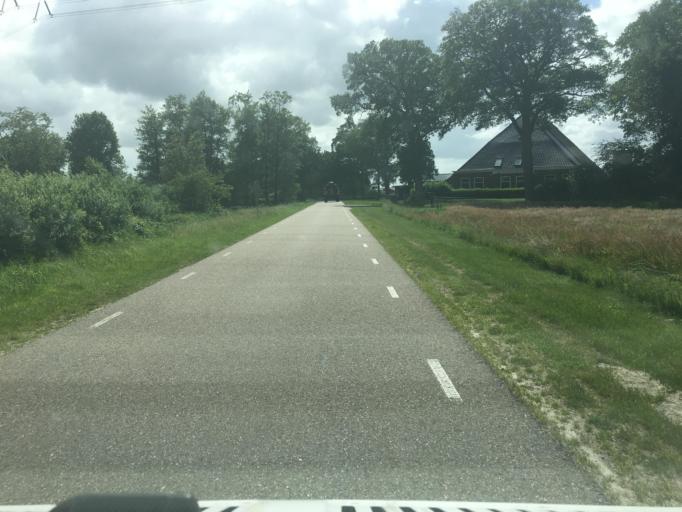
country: NL
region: Friesland
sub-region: Gemeente Heerenveen
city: Oudeschoot
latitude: 52.9163
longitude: 5.9231
